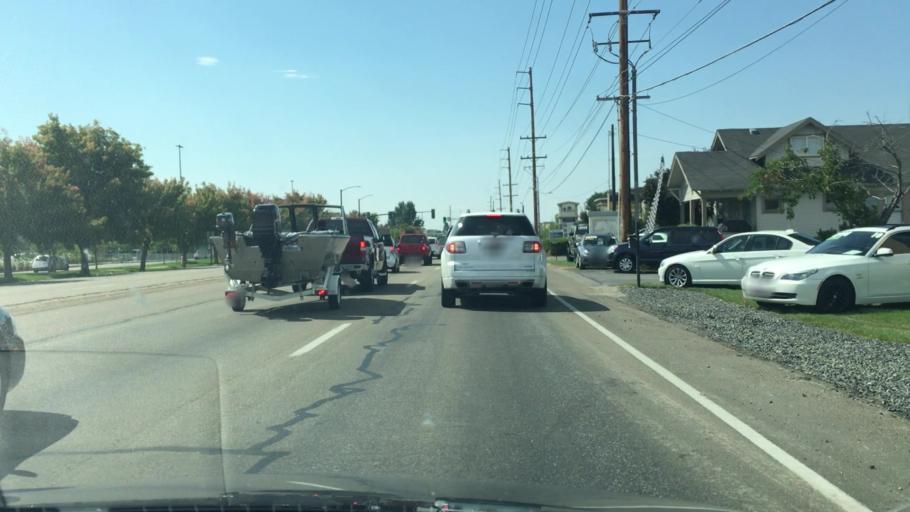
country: US
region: Idaho
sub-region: Ada County
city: Garden City
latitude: 43.6692
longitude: -116.2803
